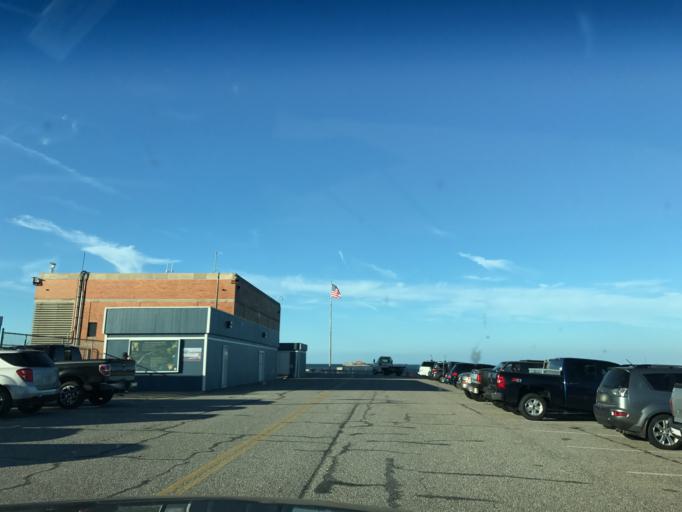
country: US
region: Virginia
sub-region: City of Virginia Beach
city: Virginia Beach
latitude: 36.9659
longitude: -76.1126
